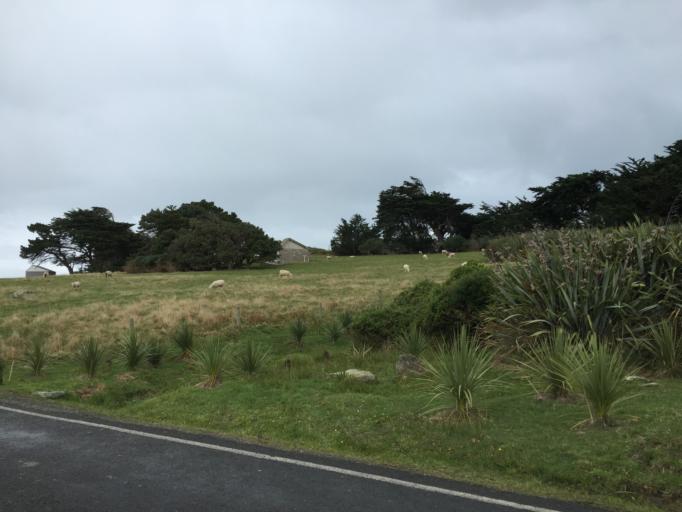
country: NZ
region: Southland
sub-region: Southland District
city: Riverton
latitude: -46.3801
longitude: 168.0332
